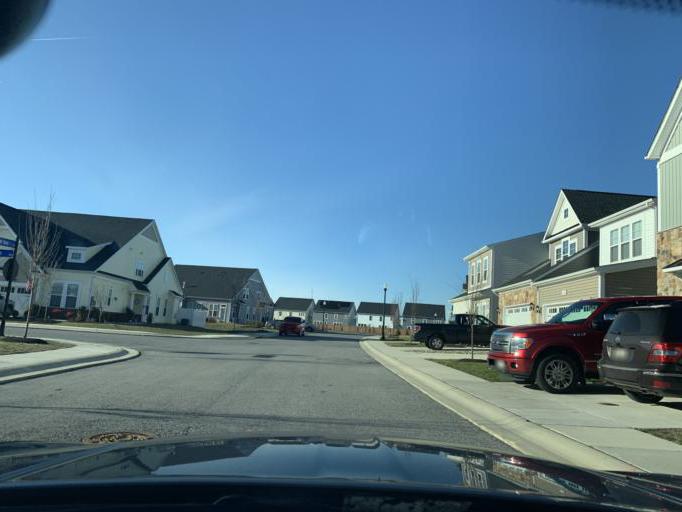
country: US
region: Maryland
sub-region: Anne Arundel County
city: Crofton
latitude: 39.0187
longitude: -76.7222
